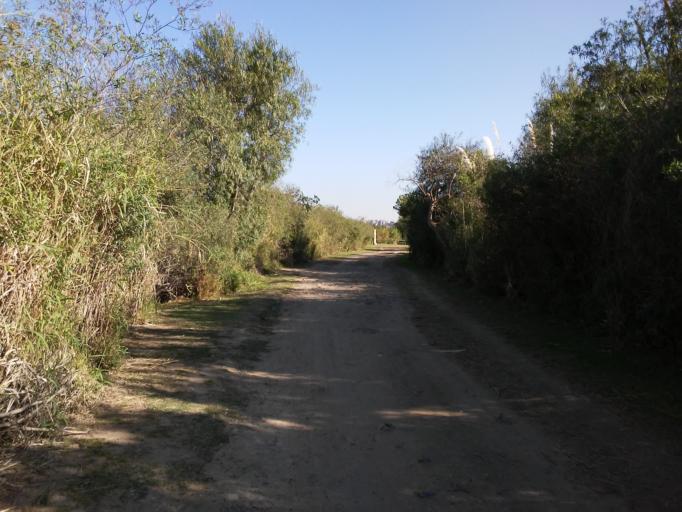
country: AR
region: Buenos Aires F.D.
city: Buenos Aires
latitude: -34.6164
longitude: -58.3405
